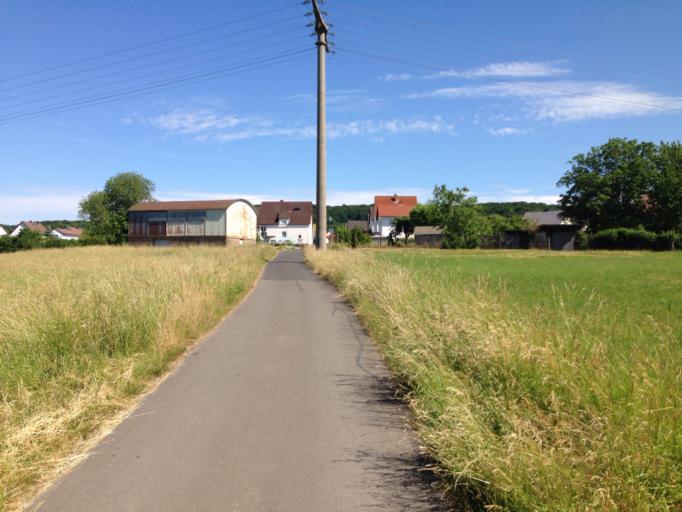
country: DE
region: Hesse
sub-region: Regierungsbezirk Giessen
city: Alten Buseck
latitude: 50.6025
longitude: 8.7444
